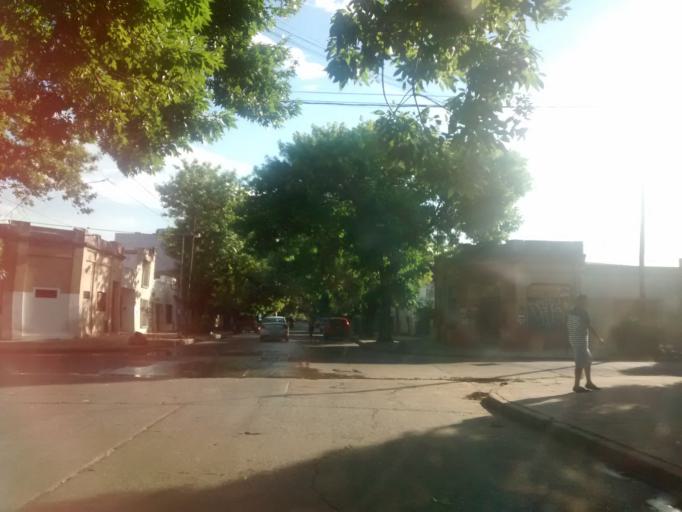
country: AR
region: Buenos Aires
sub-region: Partido de La Plata
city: La Plata
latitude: -34.9320
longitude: -57.9331
